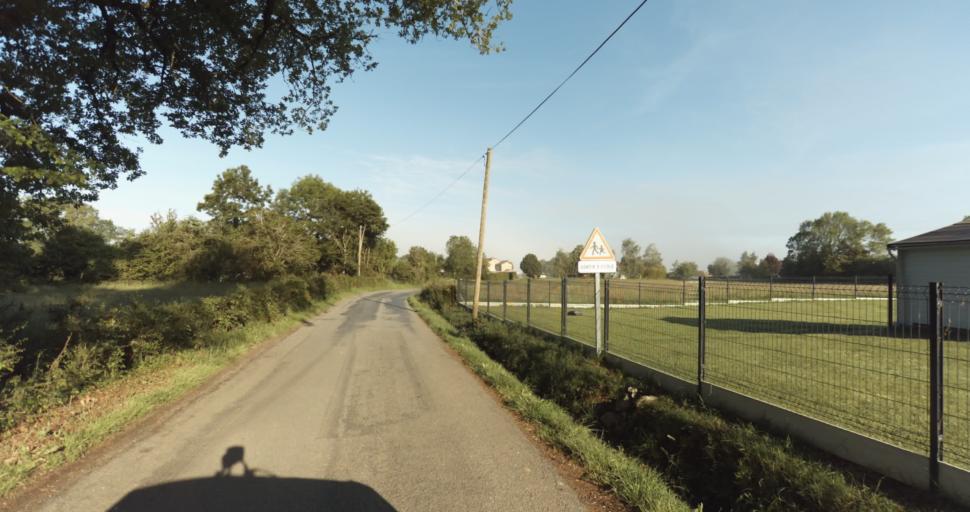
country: FR
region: Limousin
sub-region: Departement de la Haute-Vienne
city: Condat-sur-Vienne
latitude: 45.7821
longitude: 1.2857
